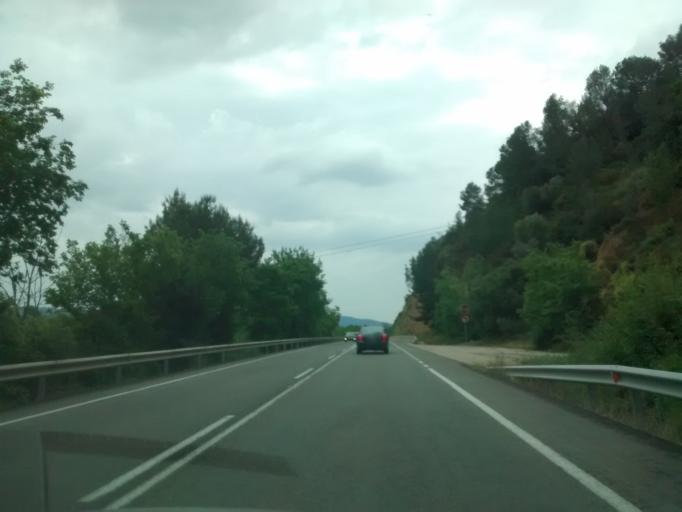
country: ES
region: Catalonia
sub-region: Provincia de Tarragona
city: Tivenys
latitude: 40.8628
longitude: 0.5075
